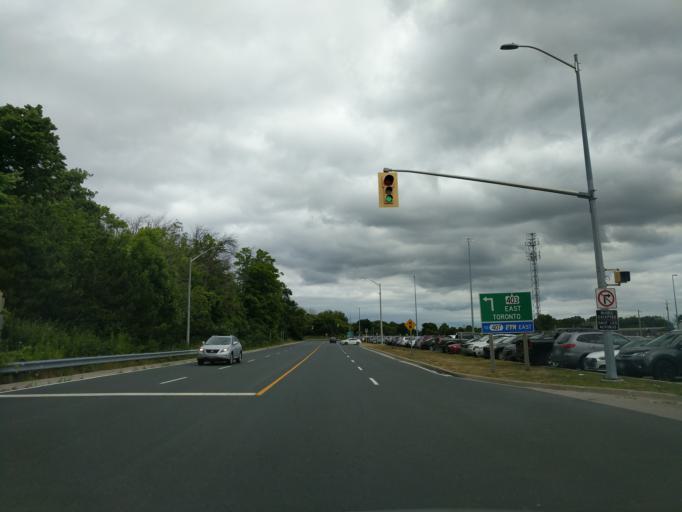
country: CA
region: Ontario
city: Hamilton
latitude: 43.3132
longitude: -79.8575
